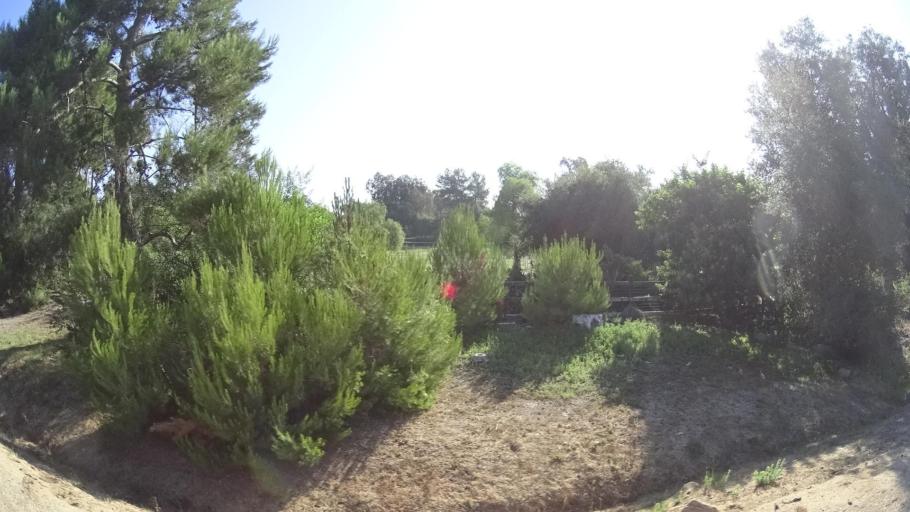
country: US
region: California
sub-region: San Diego County
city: Bonsall
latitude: 33.3081
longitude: -117.2459
